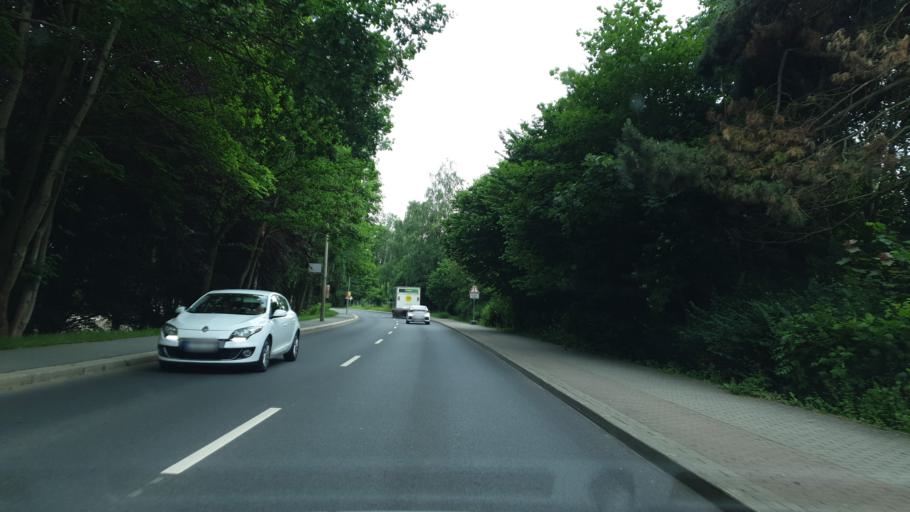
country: DE
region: Saxony
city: Rodewisch
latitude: 50.5278
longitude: 12.4006
